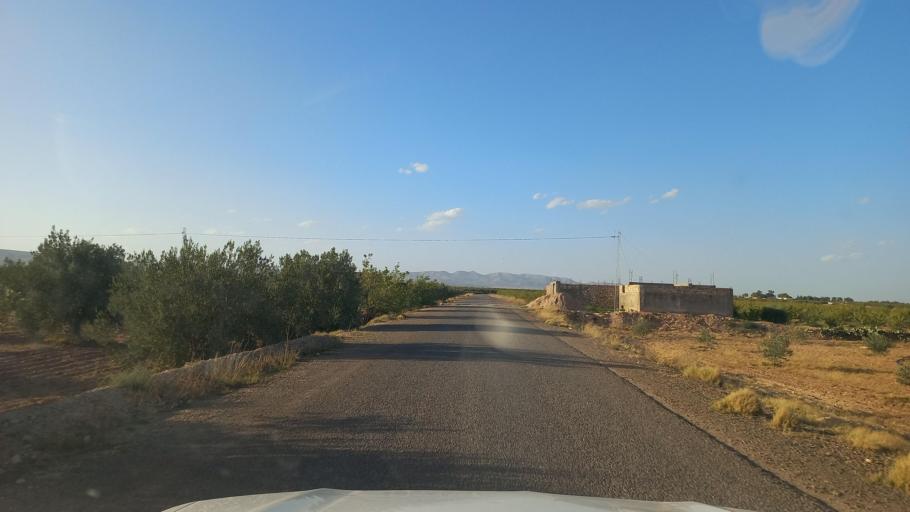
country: TN
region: Al Qasrayn
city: Kasserine
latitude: 35.2831
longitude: 9.0271
